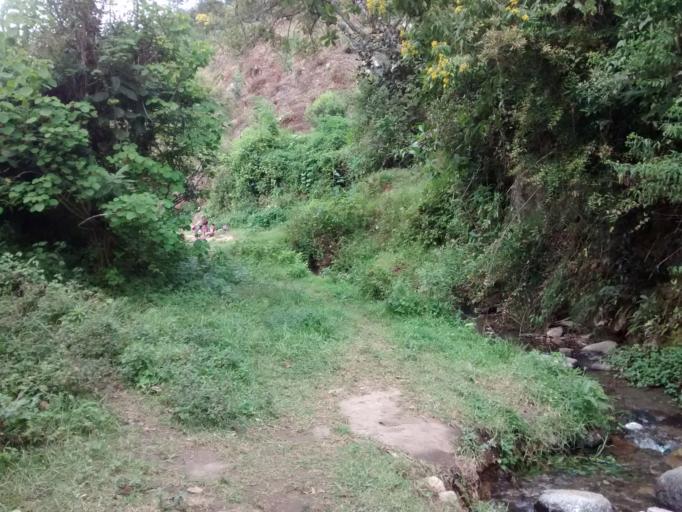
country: GT
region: Sacatepequez
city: Santo Domingo Xenacoj
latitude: 14.6976
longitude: -90.6925
